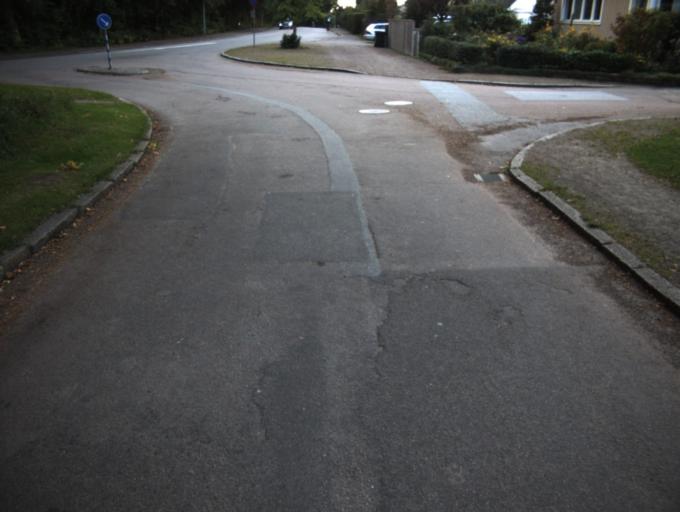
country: SE
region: Skane
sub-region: Helsingborg
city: Rydeback
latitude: 56.0236
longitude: 12.7509
